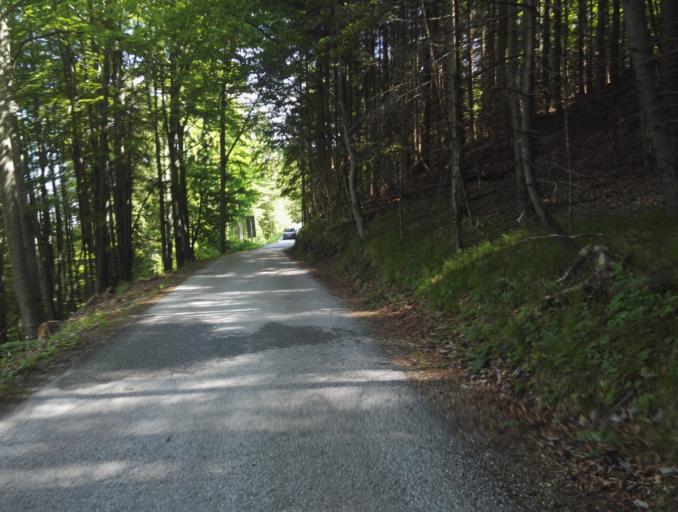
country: AT
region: Styria
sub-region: Politischer Bezirk Graz-Umgebung
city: Semriach
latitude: 47.1832
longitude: 15.4229
